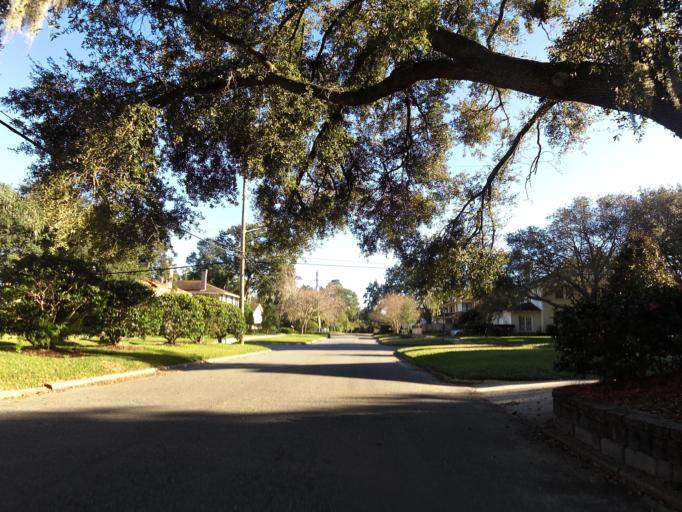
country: US
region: Florida
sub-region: Duval County
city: Jacksonville
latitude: 30.3015
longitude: -81.7018
